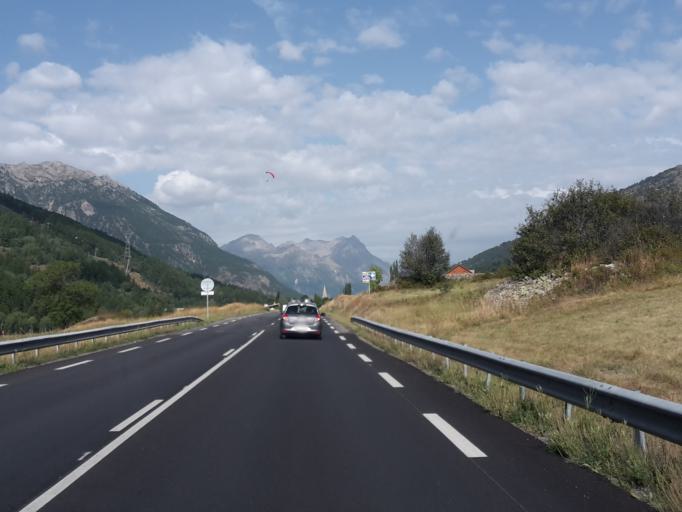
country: FR
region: Provence-Alpes-Cote d'Azur
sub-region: Departement des Hautes-Alpes
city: Saint-Chaffrey
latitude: 44.9272
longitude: 6.6005
